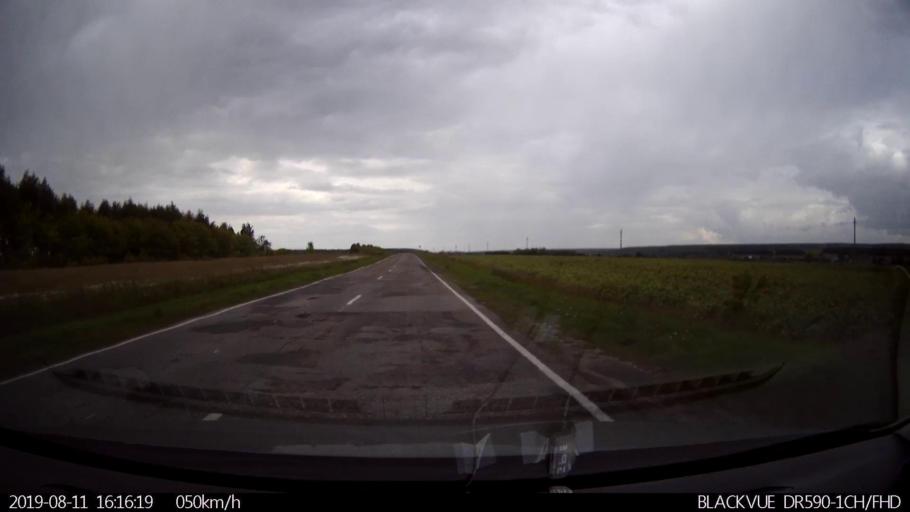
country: RU
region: Ulyanovsk
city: Mayna
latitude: 54.0402
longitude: 47.6220
